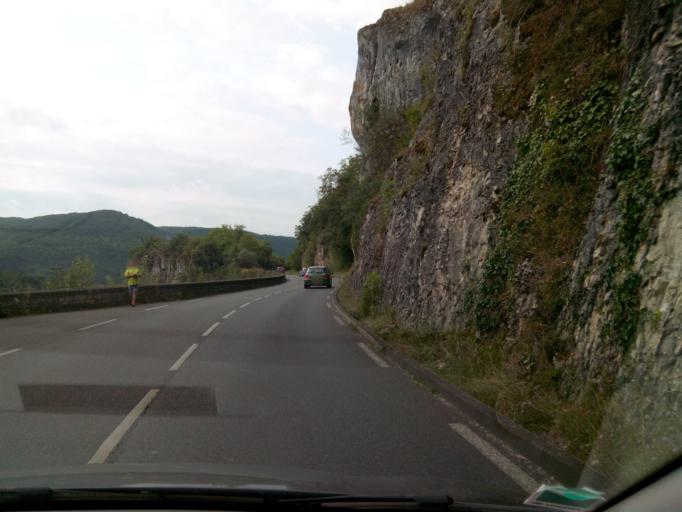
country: FR
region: Midi-Pyrenees
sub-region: Departement du Lot
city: Souillac
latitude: 44.8870
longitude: 1.4388
